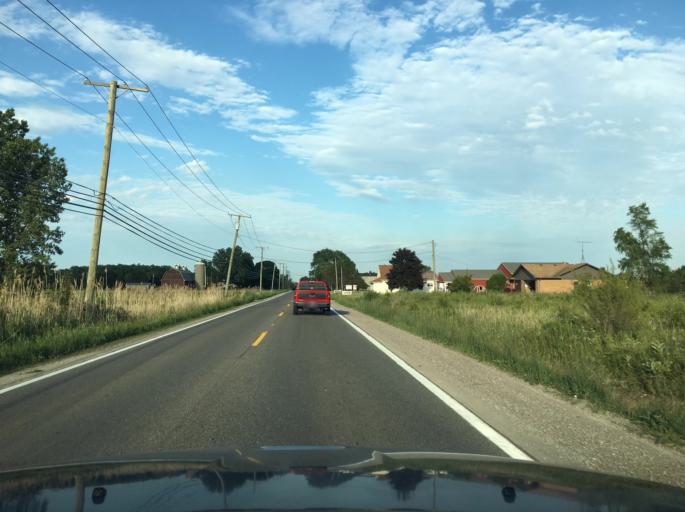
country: US
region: Michigan
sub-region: Macomb County
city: Shelby
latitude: 42.7163
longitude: -82.9557
